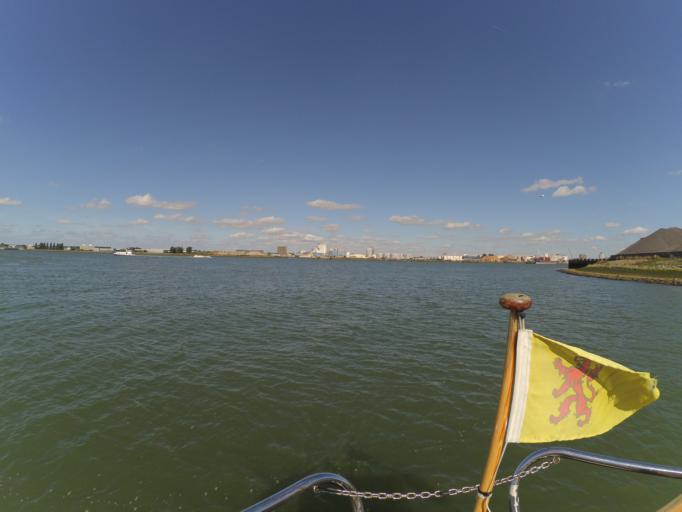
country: NL
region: South Holland
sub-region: Gemeente Vlaardingen
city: Vlaardingen
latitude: 51.8908
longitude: 4.3233
